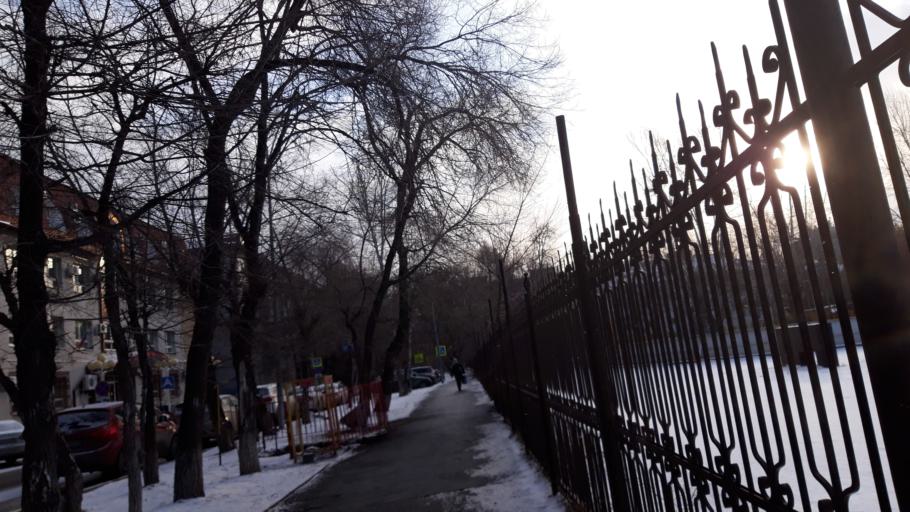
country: RU
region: Tjumen
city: Tyumen
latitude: 57.1519
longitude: 65.5489
